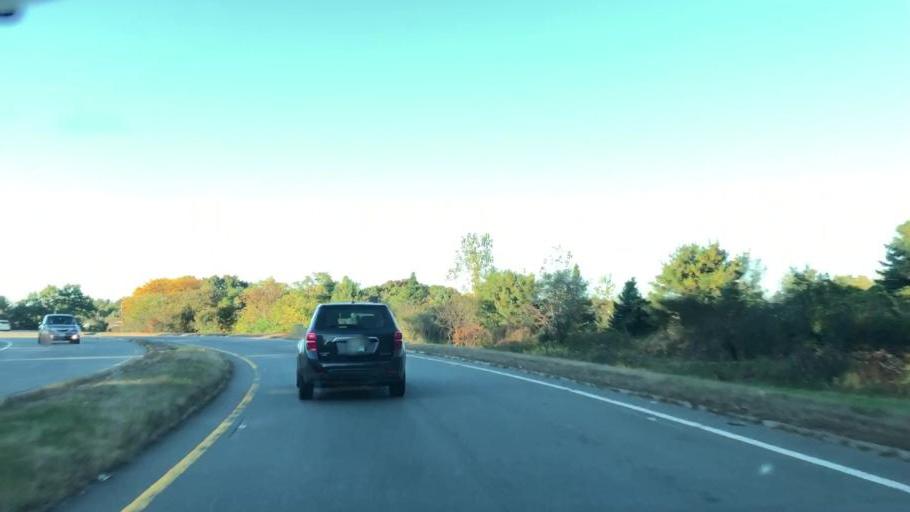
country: US
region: Massachusetts
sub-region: Essex County
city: Lawrence
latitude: 42.6637
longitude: -71.1914
